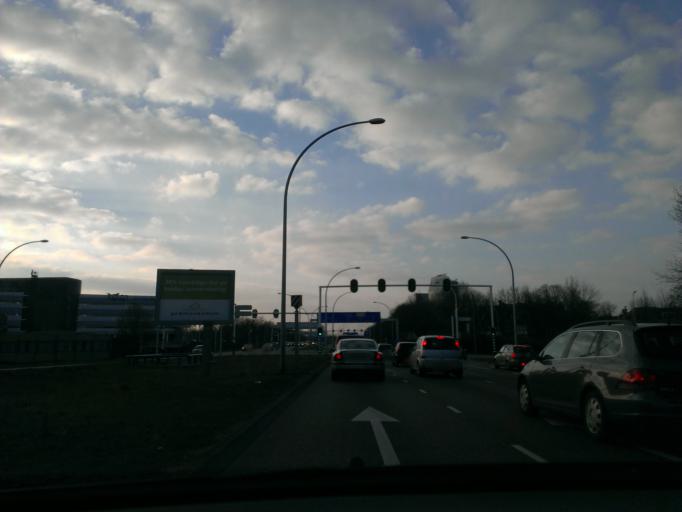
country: NL
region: Overijssel
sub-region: Gemeente Zwolle
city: Zwolle
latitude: 52.5035
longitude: 6.0740
